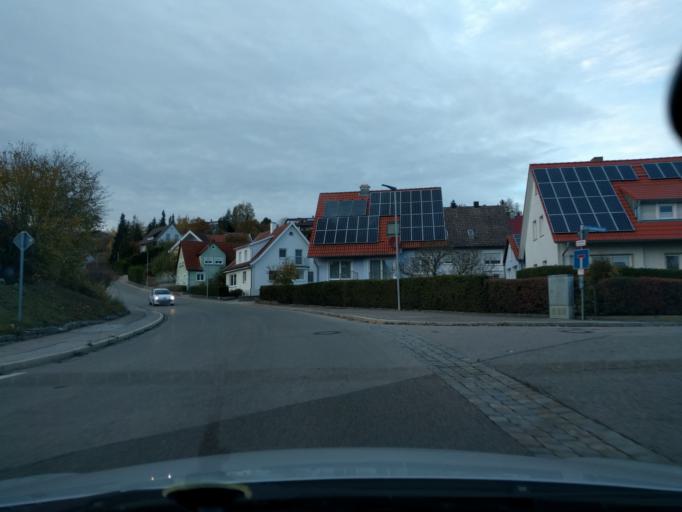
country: DE
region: Bavaria
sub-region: Regierungsbezirk Mittelfranken
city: Herrieden
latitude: 49.2370
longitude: 10.4924
